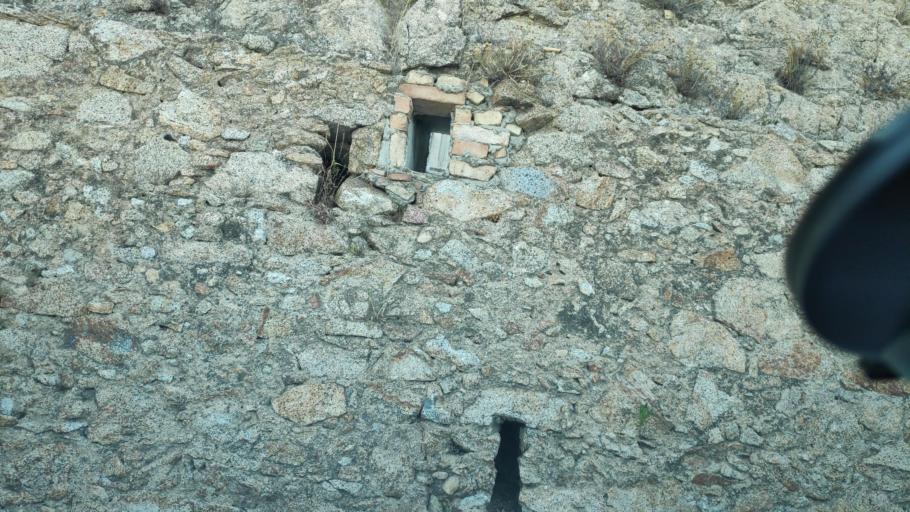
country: IT
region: Calabria
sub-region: Provincia di Catanzaro
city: Sant'Andrea Apostolo dello Ionio
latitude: 38.6201
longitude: 16.5317
